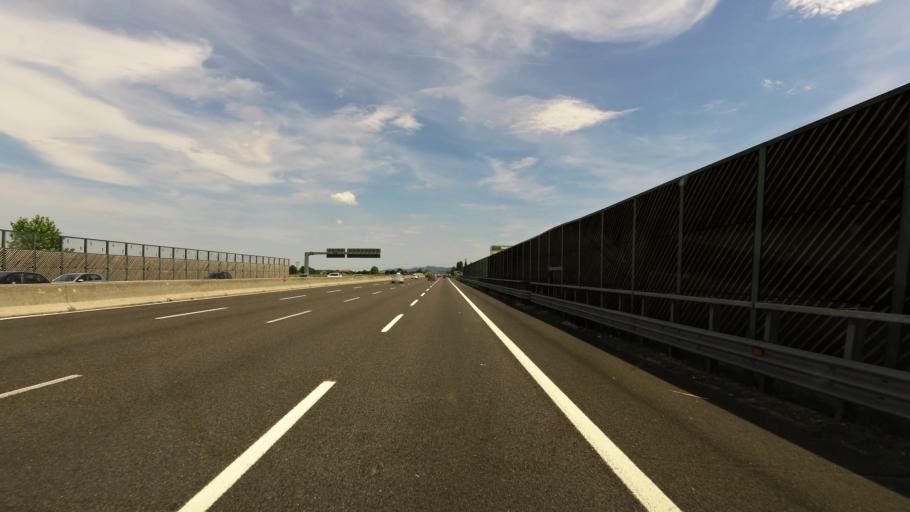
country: IT
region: Emilia-Romagna
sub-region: Provincia di Bologna
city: Crespellano
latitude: 44.5248
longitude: 11.1510
